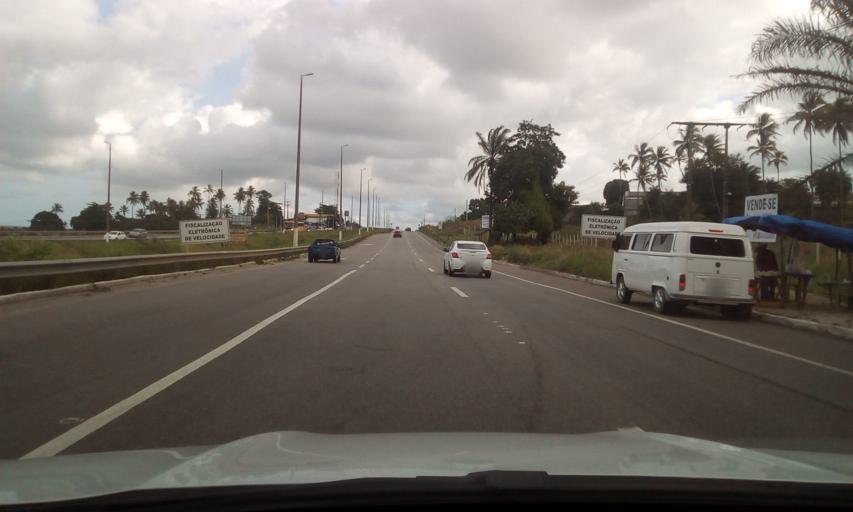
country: BR
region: Pernambuco
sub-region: Igarassu
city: Igarassu
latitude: -7.8164
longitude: -34.9178
